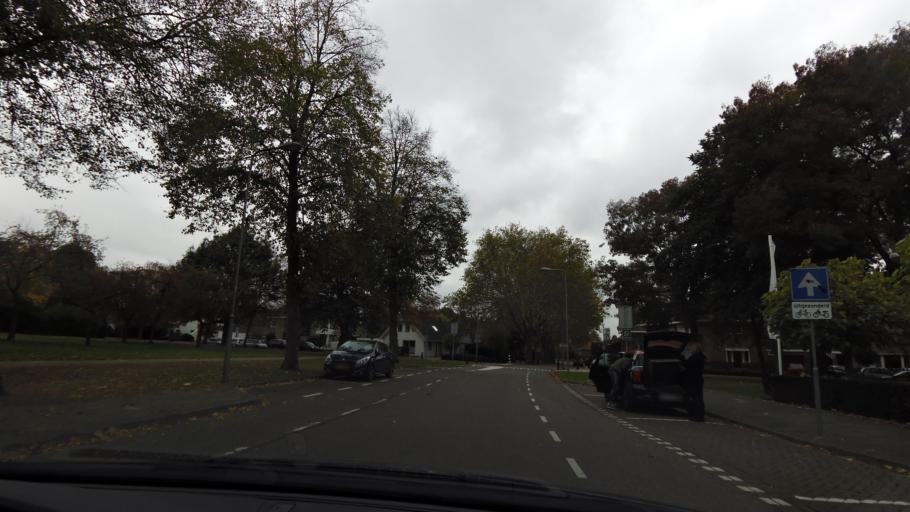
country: NL
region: Limburg
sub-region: Gemeente Sittard-Geleen
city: Sittard
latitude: 50.9943
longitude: 5.8677
